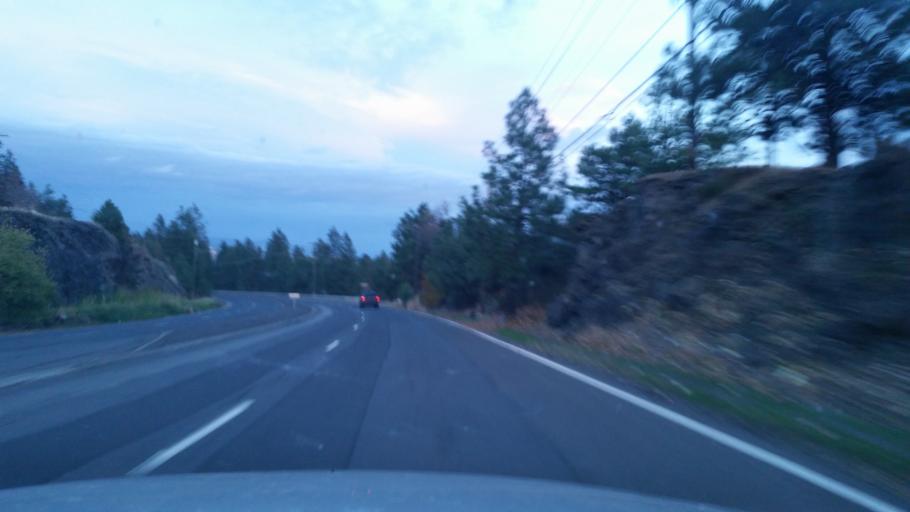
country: US
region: Washington
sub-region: Spokane County
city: Spokane
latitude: 47.6403
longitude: -117.4727
